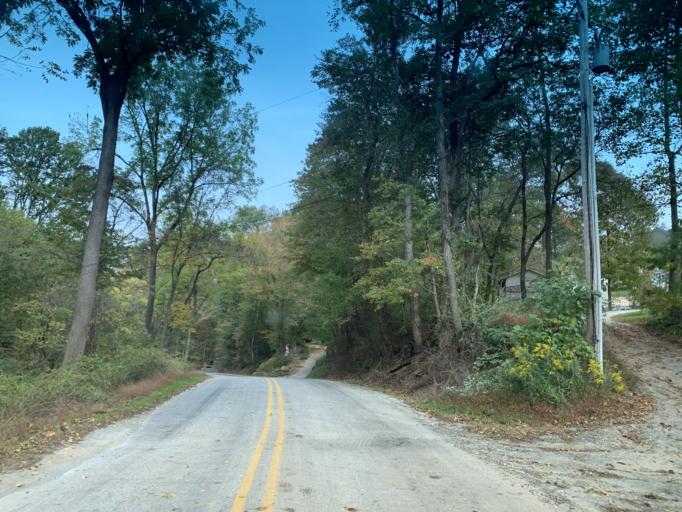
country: US
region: Pennsylvania
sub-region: York County
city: Stewartstown
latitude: 39.8199
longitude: -76.5173
